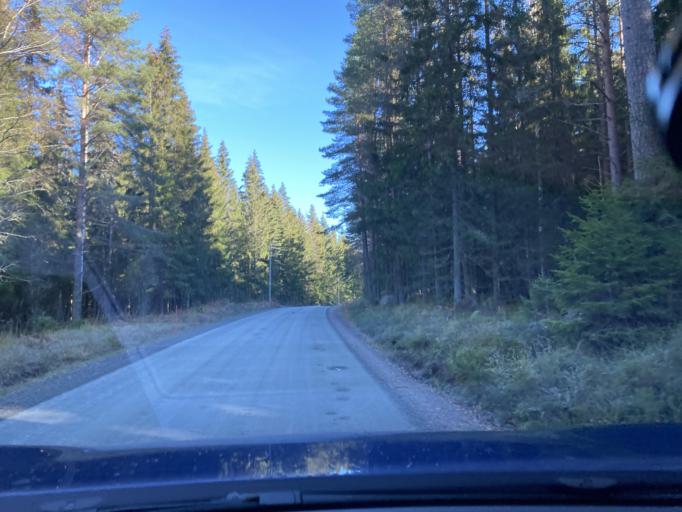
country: FI
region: Haeme
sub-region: Haemeenlinna
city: Kalvola
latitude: 60.9962
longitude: 24.1021
